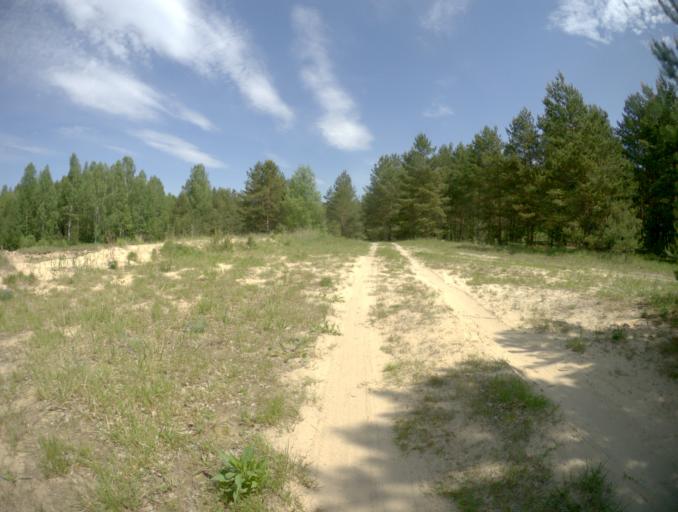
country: RU
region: Vladimir
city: Gusevskiy
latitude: 55.6862
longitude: 40.4745
